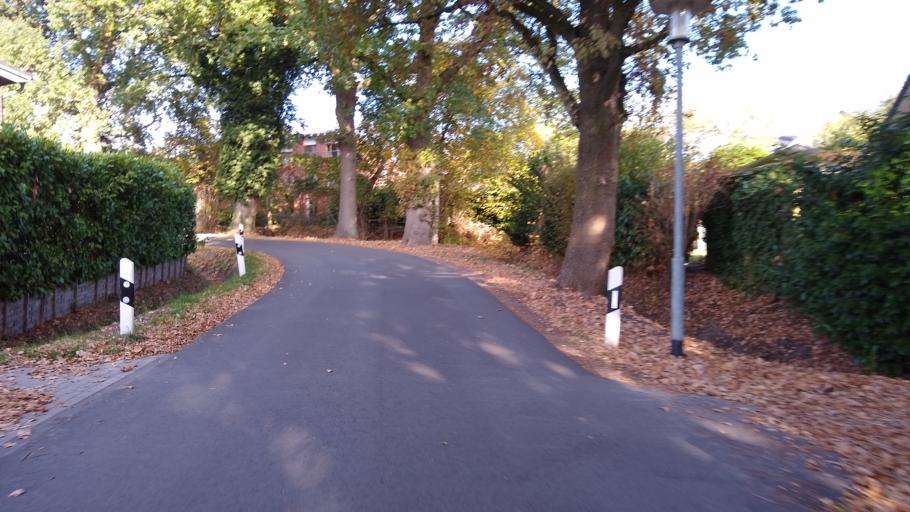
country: DE
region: Lower Saxony
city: Oldenburg
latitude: 53.1899
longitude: 8.2339
